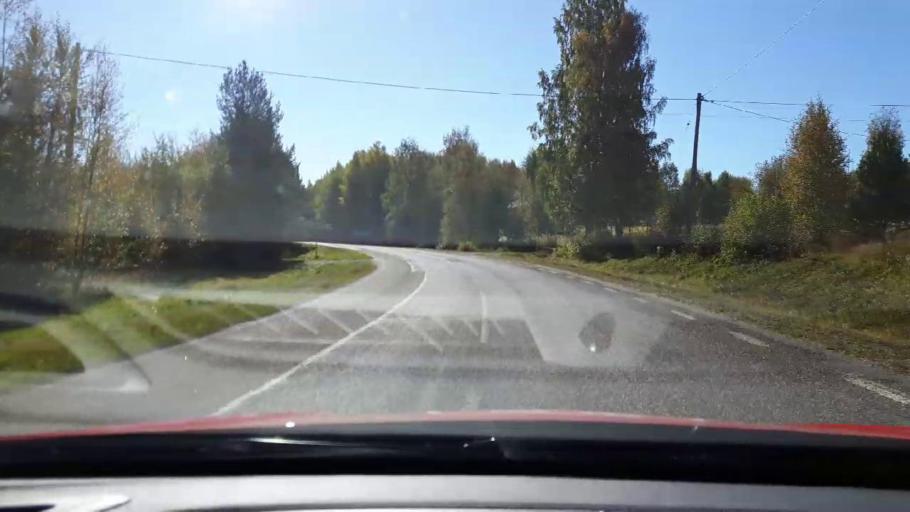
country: SE
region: Jaemtland
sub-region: Harjedalens Kommun
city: Sveg
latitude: 62.1263
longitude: 14.1632
